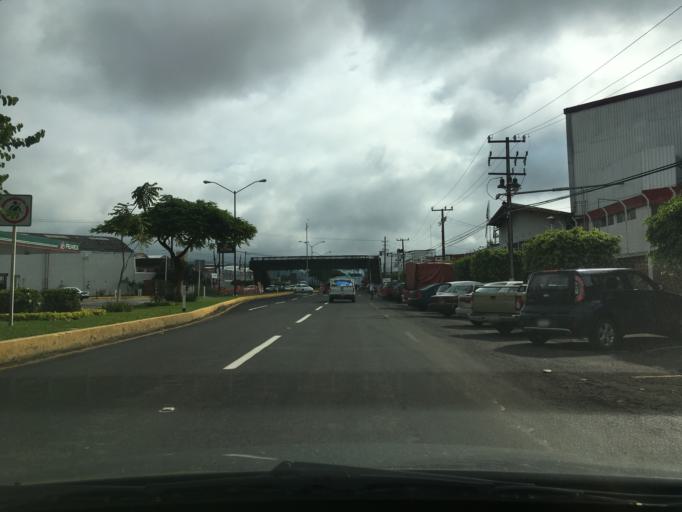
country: MX
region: Michoacan
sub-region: Uruapan
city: Uruapan
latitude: 19.4185
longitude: -102.0454
